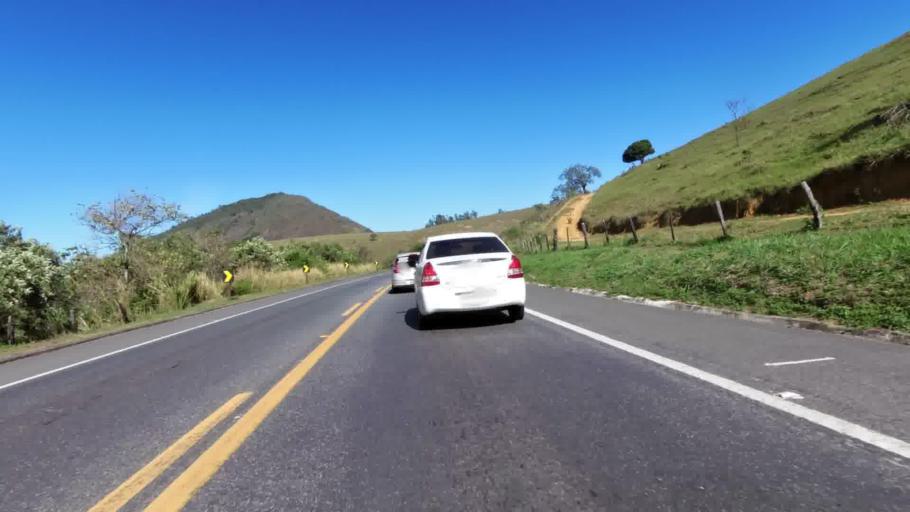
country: BR
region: Espirito Santo
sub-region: Alfredo Chaves
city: Alfredo Chaves
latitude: -20.6936
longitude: -40.6883
